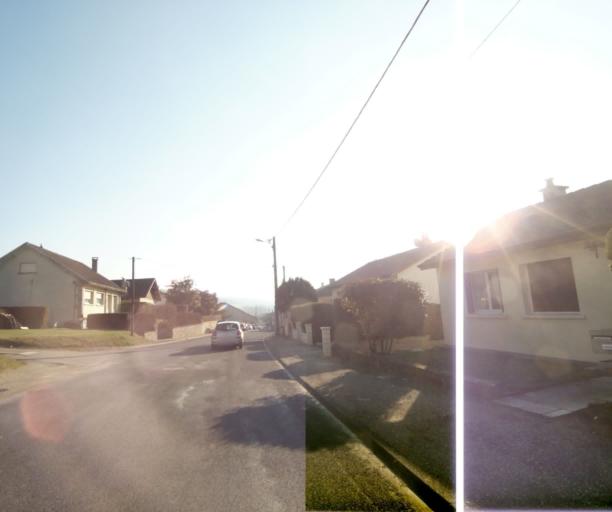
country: FR
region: Champagne-Ardenne
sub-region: Departement de la Haute-Marne
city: Chevillon
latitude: 48.4946
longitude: 5.1347
